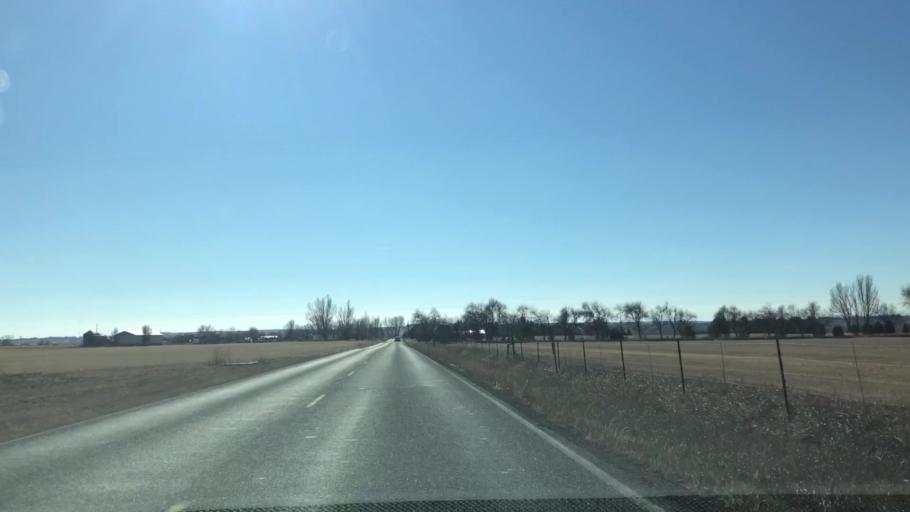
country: US
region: Colorado
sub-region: Weld County
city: Windsor
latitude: 40.4959
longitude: -104.9442
